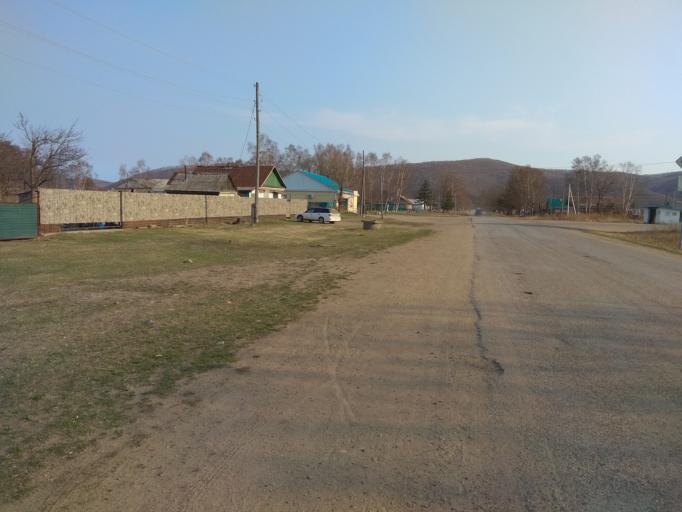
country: RU
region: Primorskiy
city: Lazo
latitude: 43.3082
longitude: 134.6040
